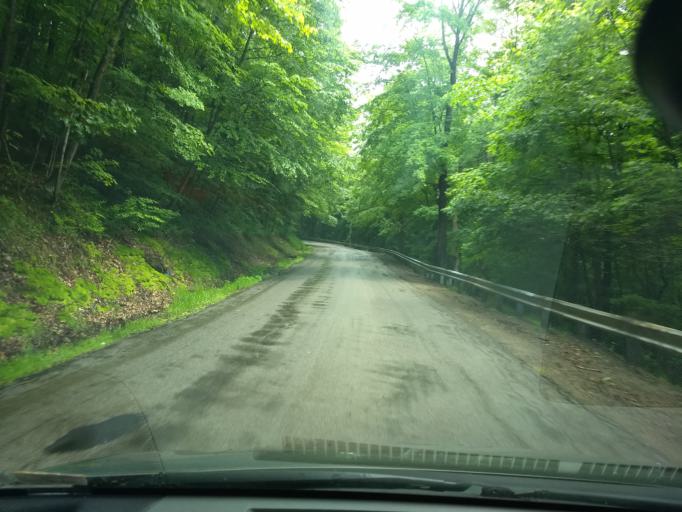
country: US
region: Pennsylvania
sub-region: Armstrong County
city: Orchard Hills
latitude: 40.5648
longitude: -79.5145
